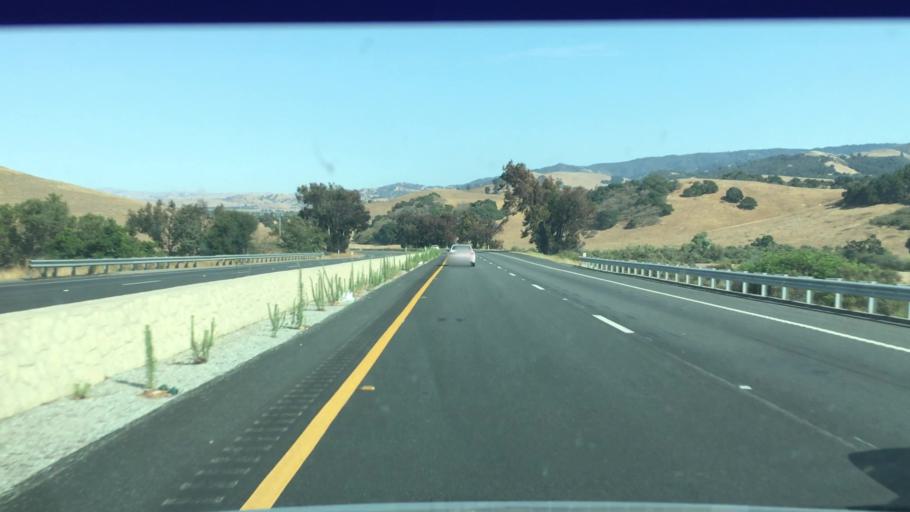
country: US
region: California
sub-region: San Benito County
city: San Juan Bautista
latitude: 36.8499
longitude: -121.5614
